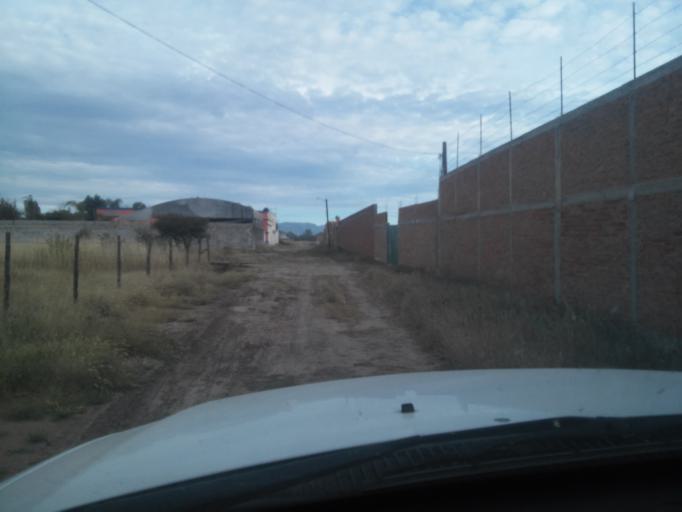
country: MX
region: Durango
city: Victoria de Durango
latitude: 24.0240
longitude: -104.5841
